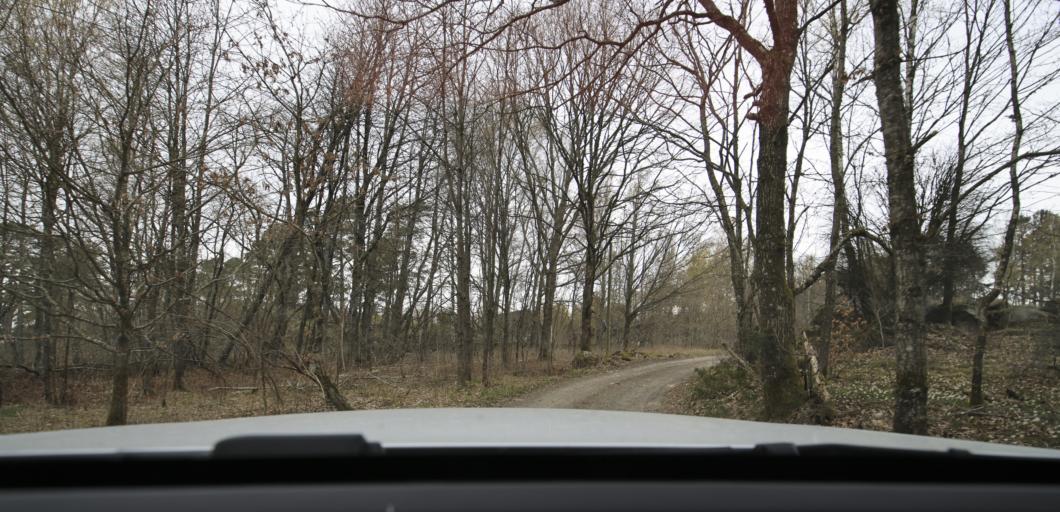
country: SE
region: Halland
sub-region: Varbergs Kommun
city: Tvaaker
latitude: 57.1241
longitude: 12.4585
